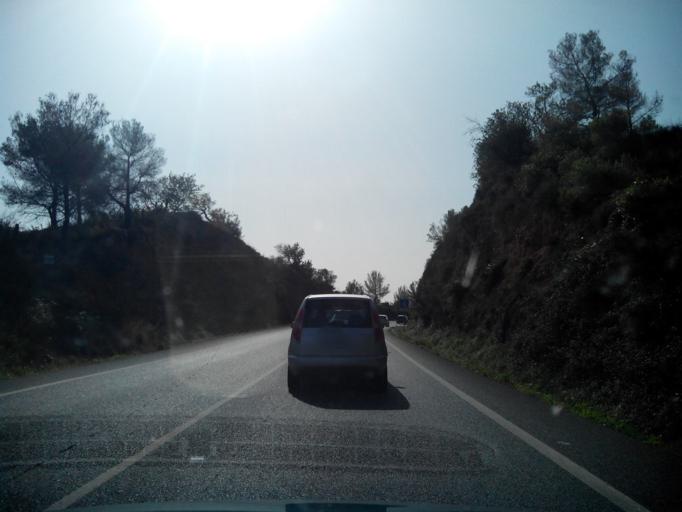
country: ES
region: Catalonia
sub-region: Provincia de Tarragona
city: Alcover
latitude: 41.2891
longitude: 1.1881
